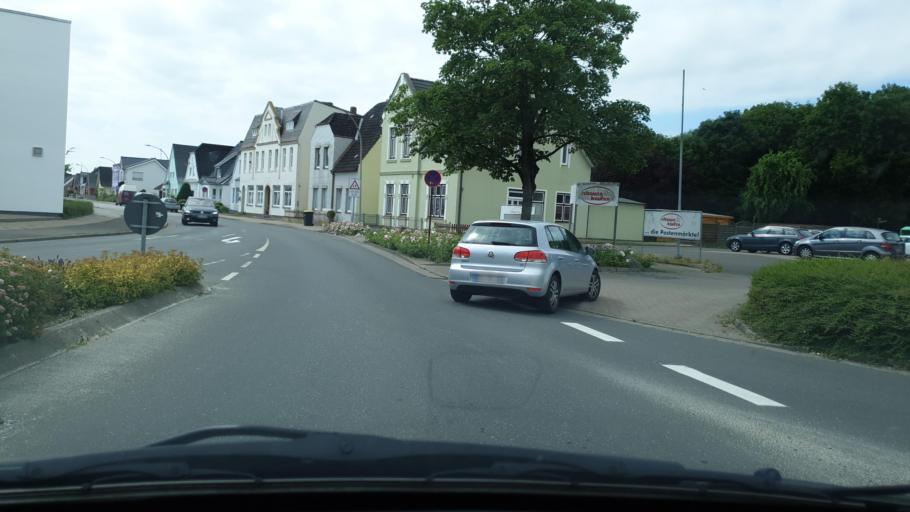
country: DE
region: Schleswig-Holstein
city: Helse
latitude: 53.9513
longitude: 9.0084
